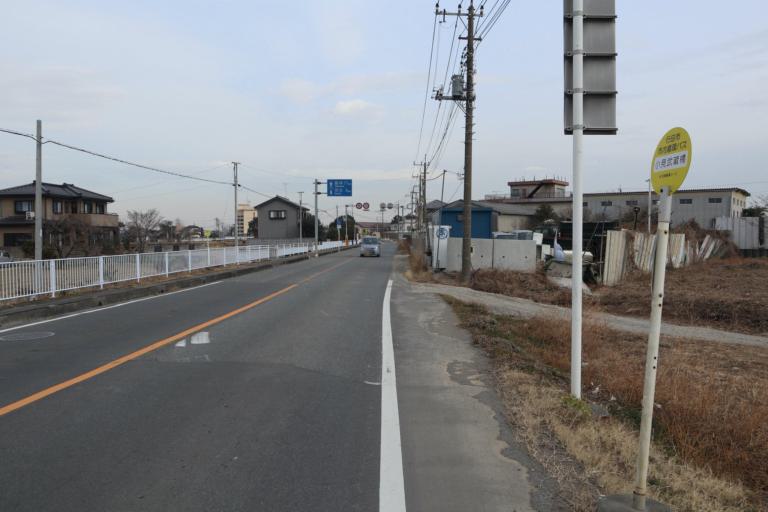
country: JP
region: Saitama
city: Gyoda
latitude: 36.1612
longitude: 139.4805
